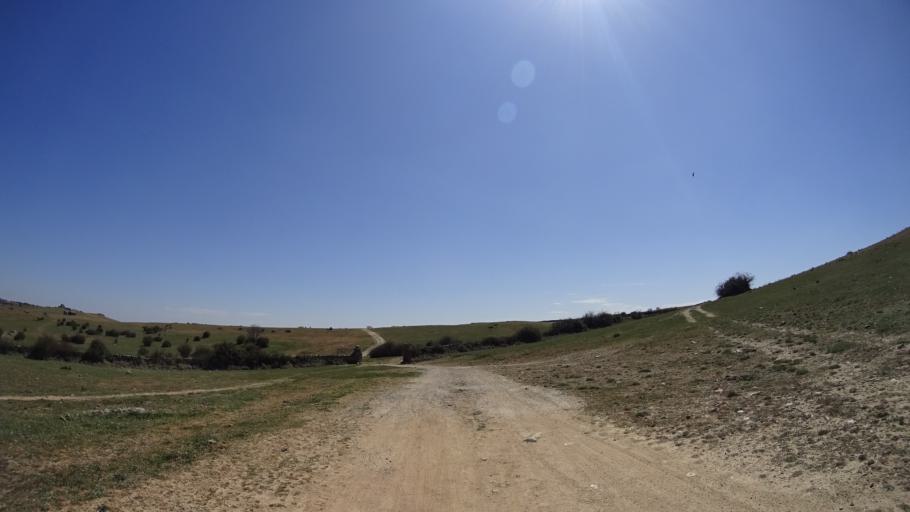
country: ES
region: Madrid
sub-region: Provincia de Madrid
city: Colmenar Viejo
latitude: 40.6928
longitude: -3.7571
